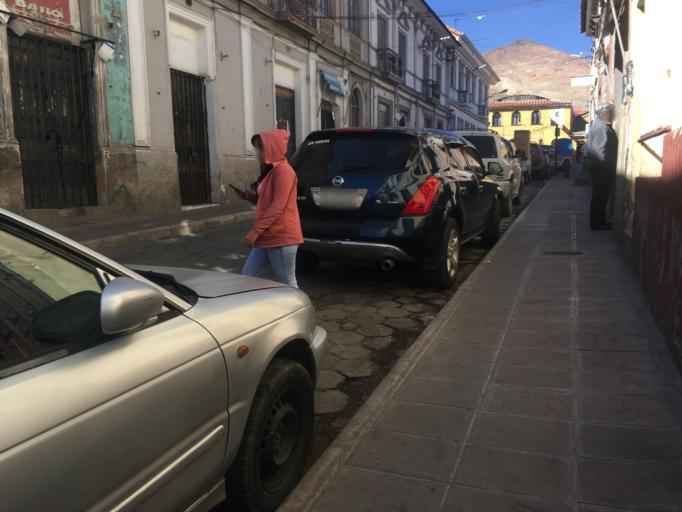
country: BO
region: Potosi
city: Potosi
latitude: -19.5863
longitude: -65.7552
